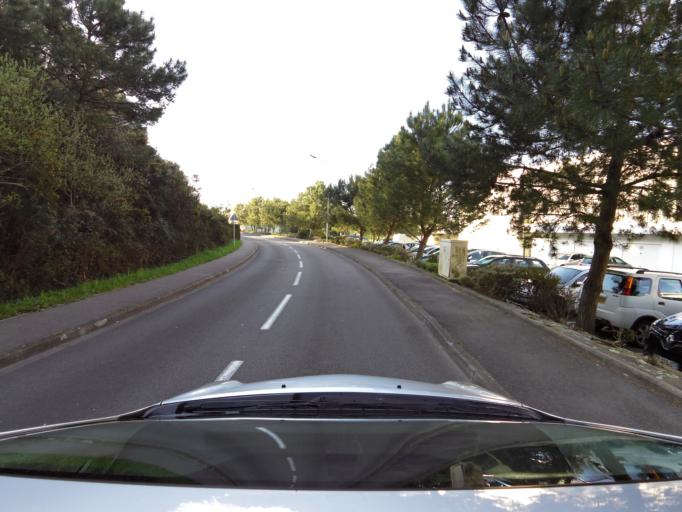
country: FR
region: Brittany
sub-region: Departement du Morbihan
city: Larmor-Plage
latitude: 47.7292
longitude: -3.3869
